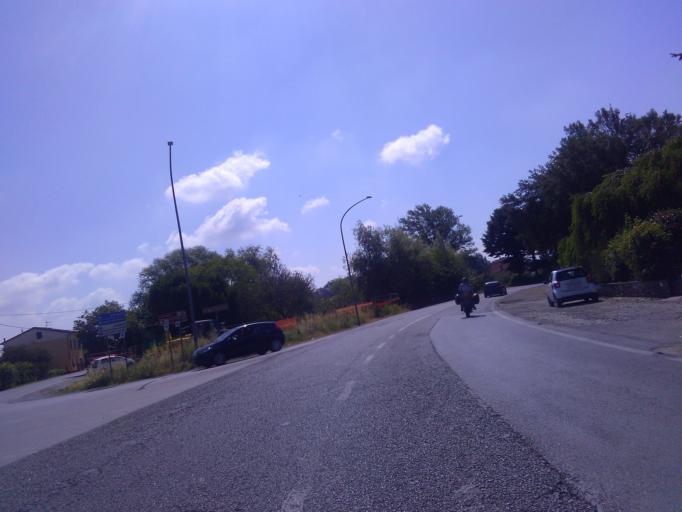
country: IT
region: Tuscany
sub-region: Provincia di Lucca
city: Lucca
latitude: 43.8563
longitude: 10.4447
